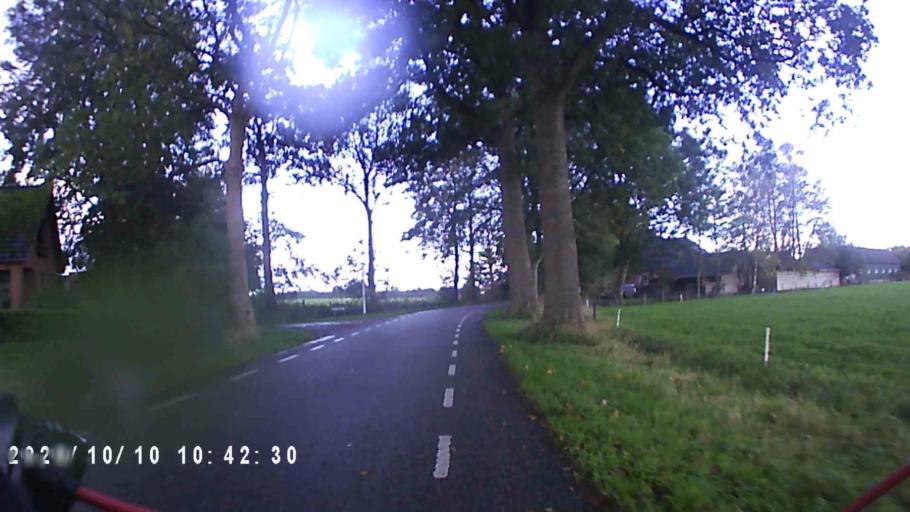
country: NL
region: Groningen
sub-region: Gemeente Grootegast
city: Grootegast
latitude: 53.1742
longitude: 6.2739
